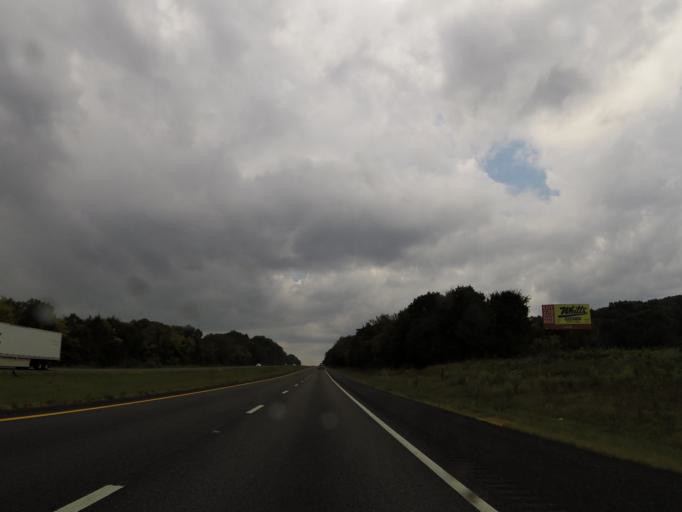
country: US
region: Tennessee
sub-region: Wilson County
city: Watertown
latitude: 36.1788
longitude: -86.1453
